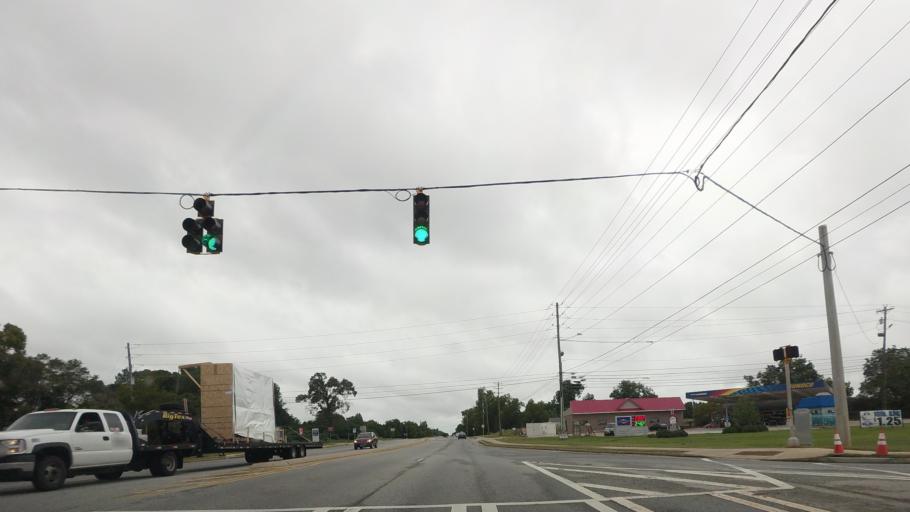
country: US
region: Georgia
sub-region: Houston County
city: Perry
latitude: 32.5058
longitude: -83.6625
